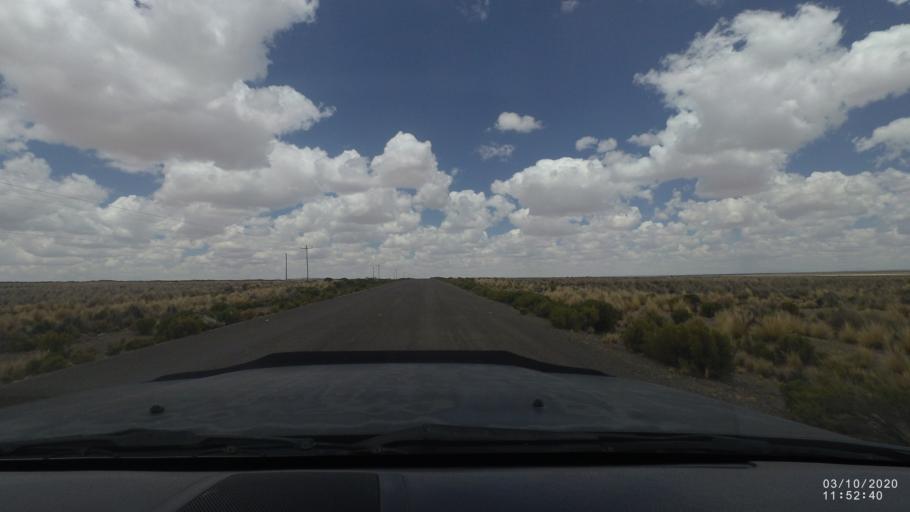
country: BO
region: Oruro
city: Poopo
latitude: -18.4647
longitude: -67.6007
